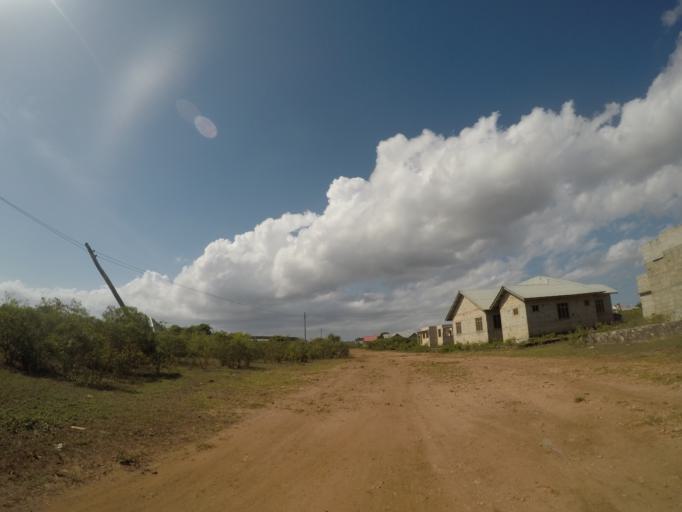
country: TZ
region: Zanzibar Central/South
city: Koani
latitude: -6.2103
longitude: 39.2935
